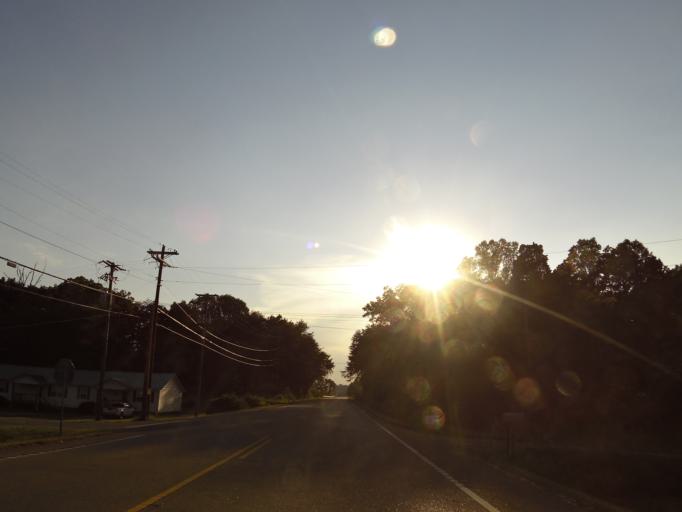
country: US
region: Tennessee
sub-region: McMinn County
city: Englewood
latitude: 35.4253
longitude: -84.5397
